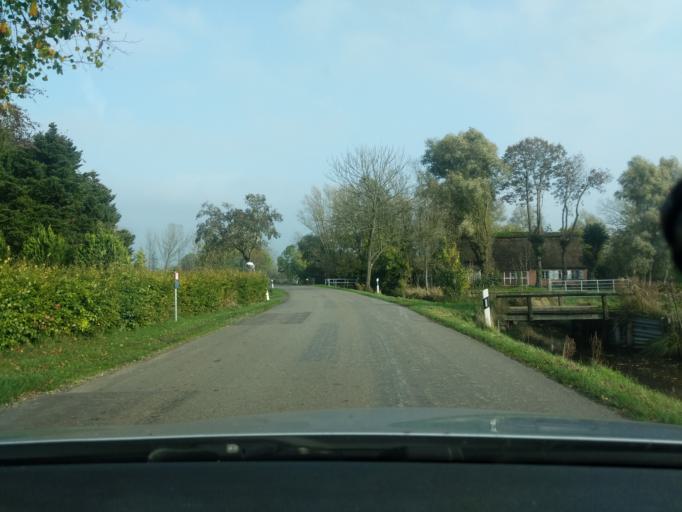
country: DE
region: Lower Saxony
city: Nordleda
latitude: 53.7305
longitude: 8.8617
